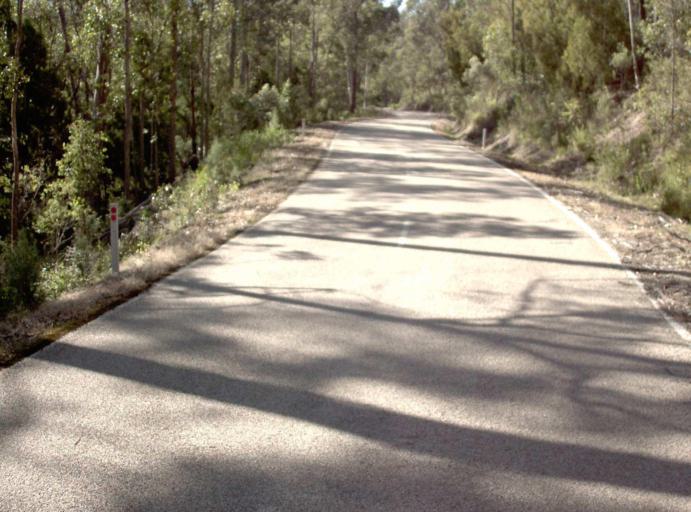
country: AU
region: Victoria
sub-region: East Gippsland
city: Lakes Entrance
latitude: -37.5600
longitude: 148.5550
